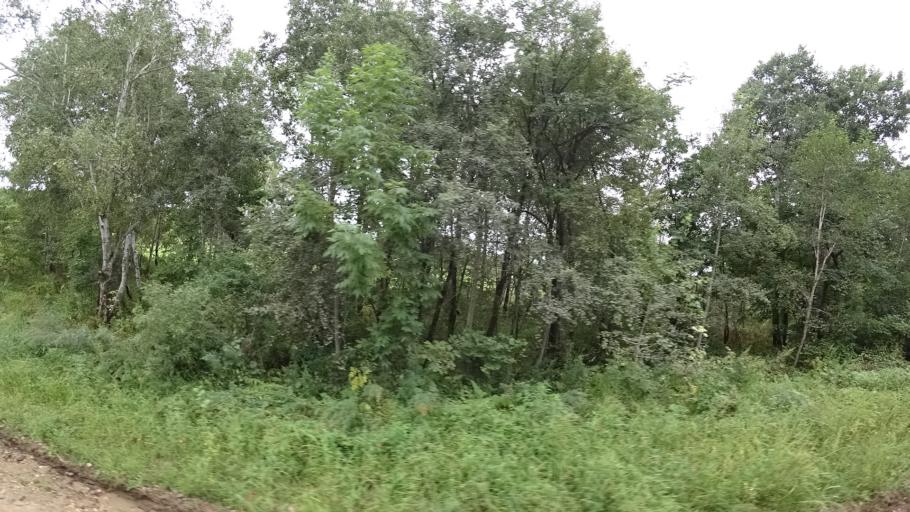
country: RU
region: Primorskiy
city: Rettikhovka
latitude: 44.0645
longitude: 132.6519
